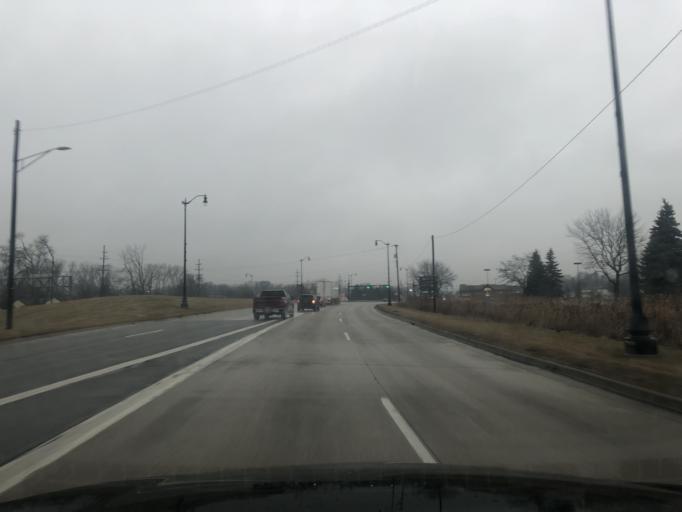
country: US
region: Michigan
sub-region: Wayne County
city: Taylor
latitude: 42.1941
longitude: -83.2668
